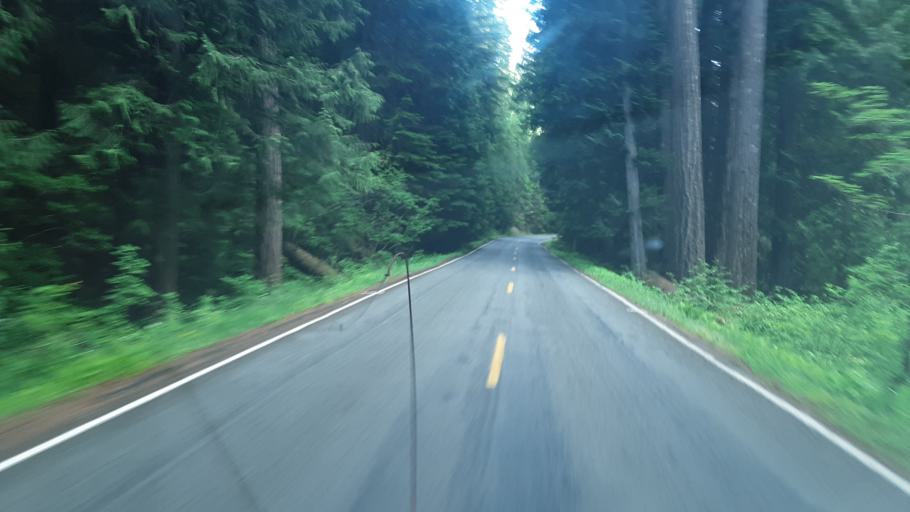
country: US
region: Washington
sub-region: Pierce County
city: Buckley
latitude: 46.7647
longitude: -121.5489
